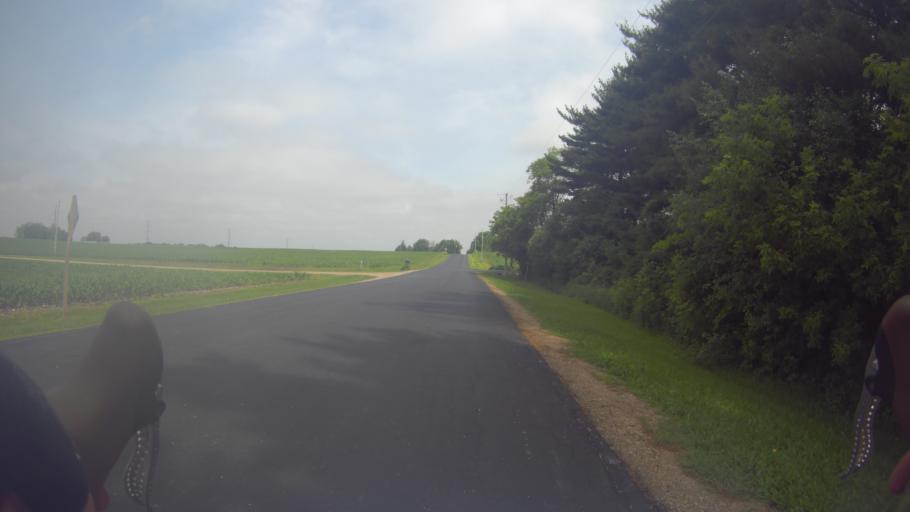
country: US
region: Wisconsin
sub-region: Rock County
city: Edgerton
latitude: 42.8980
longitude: -89.0426
